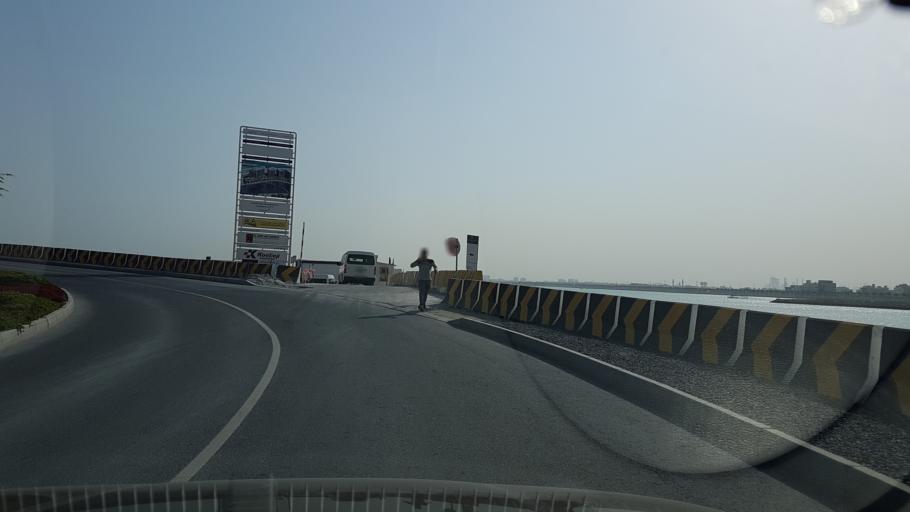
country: BH
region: Muharraq
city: Al Hadd
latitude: 26.2700
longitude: 50.6669
